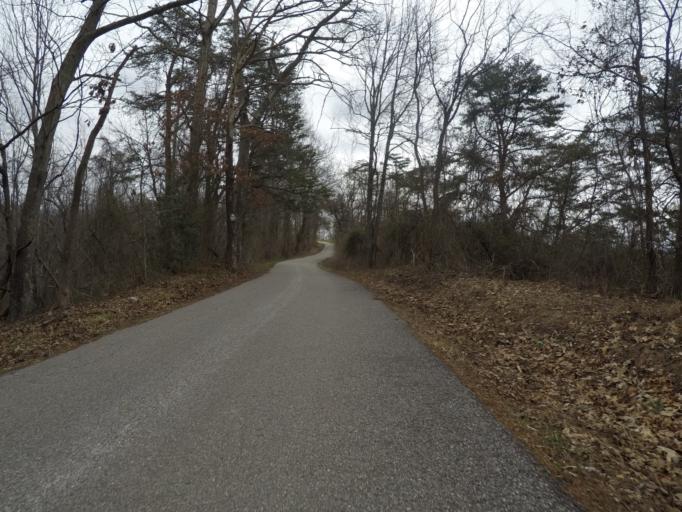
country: US
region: West Virginia
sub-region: Wayne County
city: Lavalette
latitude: 38.3683
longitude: -82.4247
